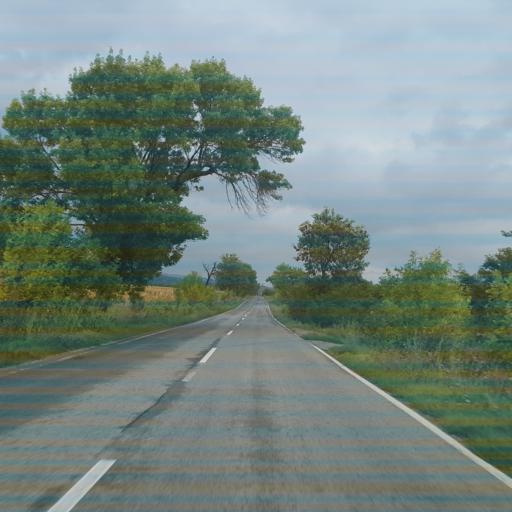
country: RS
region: Central Serbia
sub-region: Nisavski Okrug
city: Aleksinac
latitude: 43.5917
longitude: 21.6380
